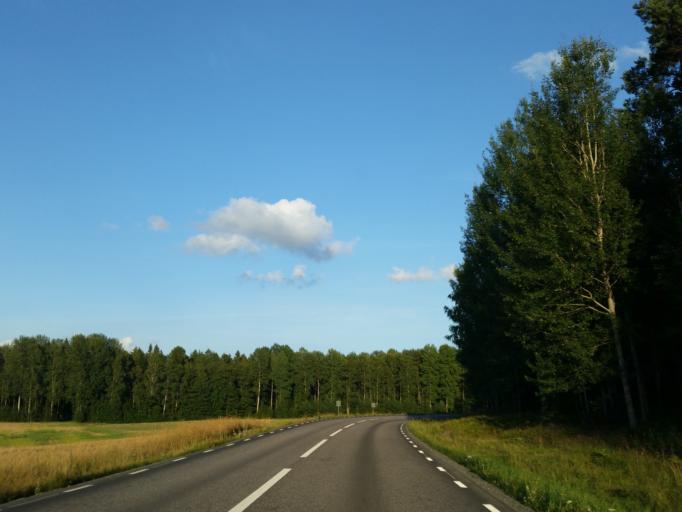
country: SE
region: Stockholm
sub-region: Sodertalje Kommun
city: Soedertaelje
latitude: 59.2489
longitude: 17.5323
